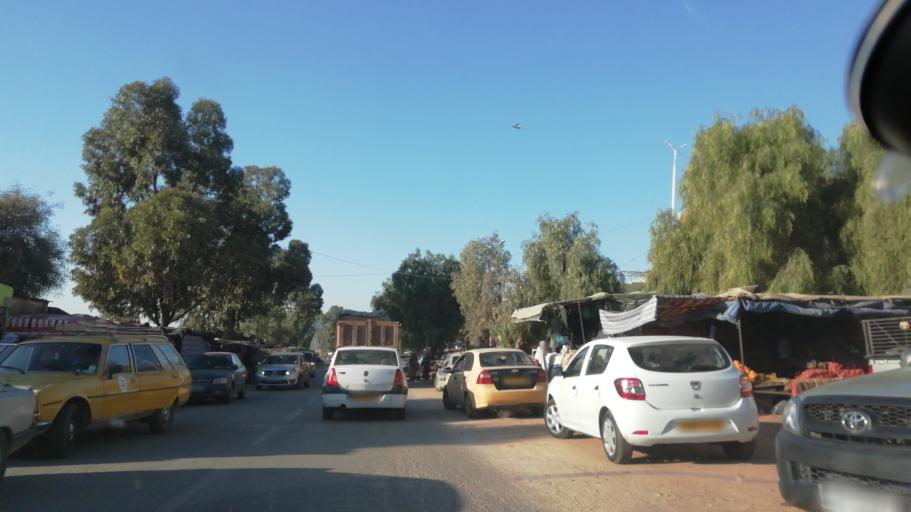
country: DZ
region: Tlemcen
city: Remchi
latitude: 35.0561
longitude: -1.4991
